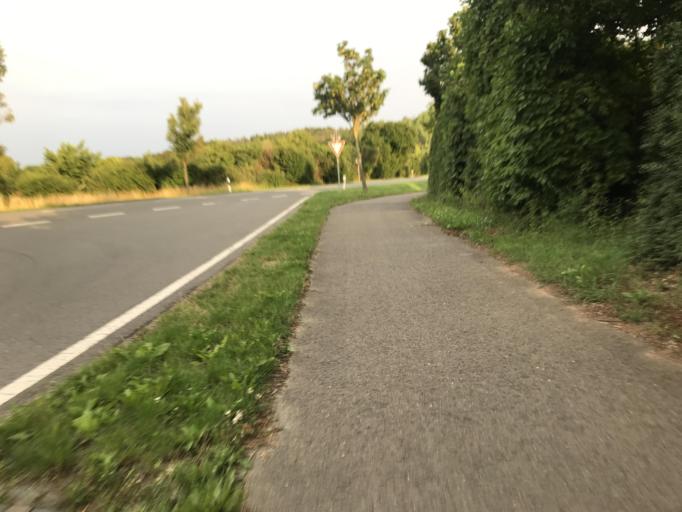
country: DE
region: Saxony-Anhalt
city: Quedlinburg
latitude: 51.8054
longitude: 11.1303
